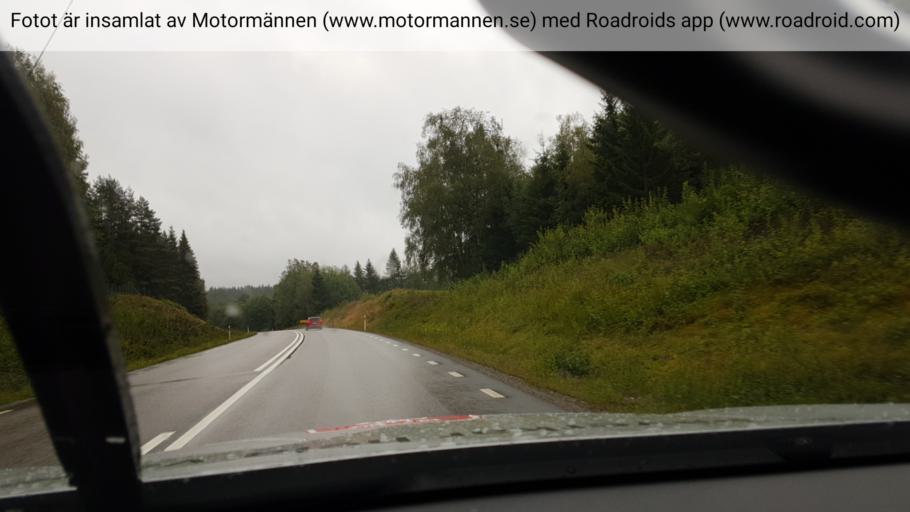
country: SE
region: Vaestra Goetaland
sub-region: Bengtsfors Kommun
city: Dals Langed
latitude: 59.0294
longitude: 12.4016
